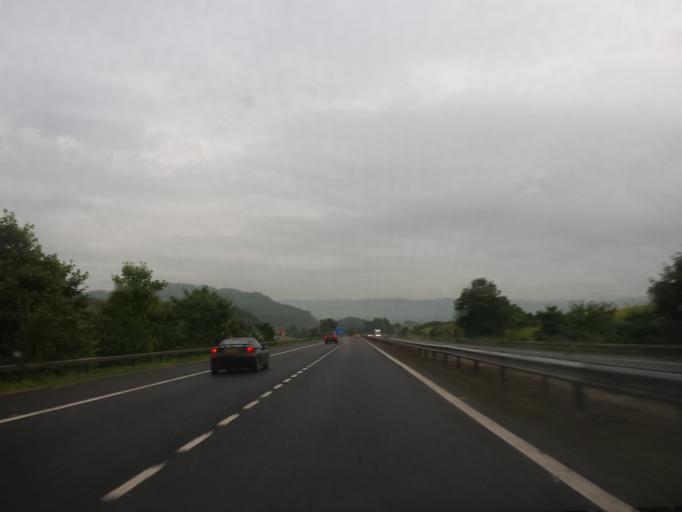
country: GB
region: Scotland
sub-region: Perth and Kinross
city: Perth
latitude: 56.3726
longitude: -3.4422
